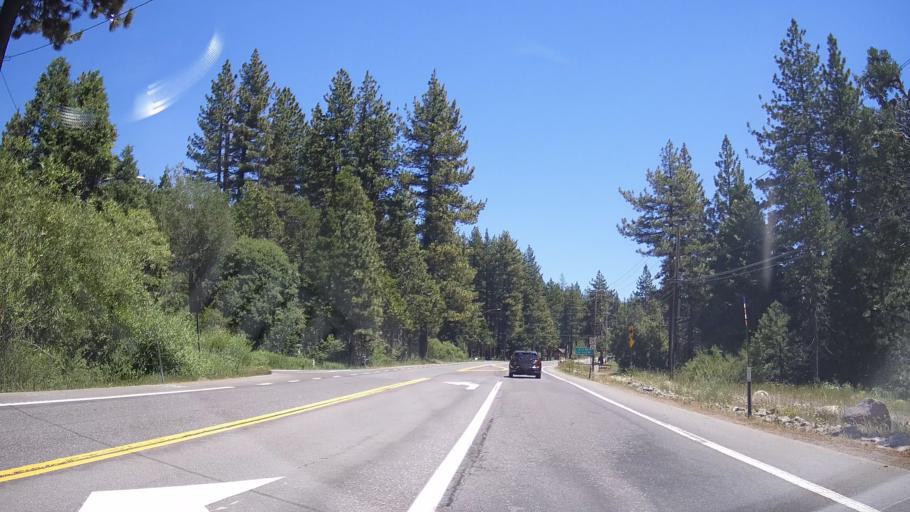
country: US
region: California
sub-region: Placer County
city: Dollar Point
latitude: 39.1889
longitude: -120.1160
